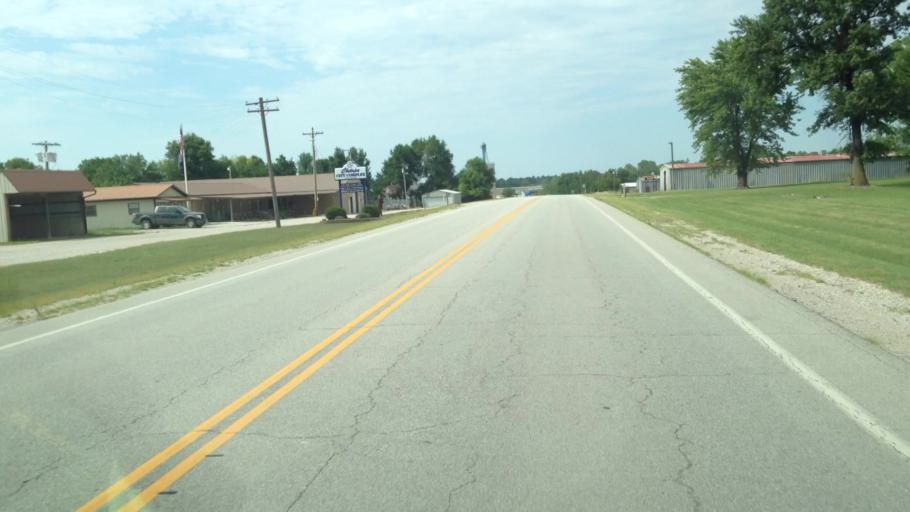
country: US
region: Kansas
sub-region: Labette County
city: Chetopa
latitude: 37.0422
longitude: -95.1002
